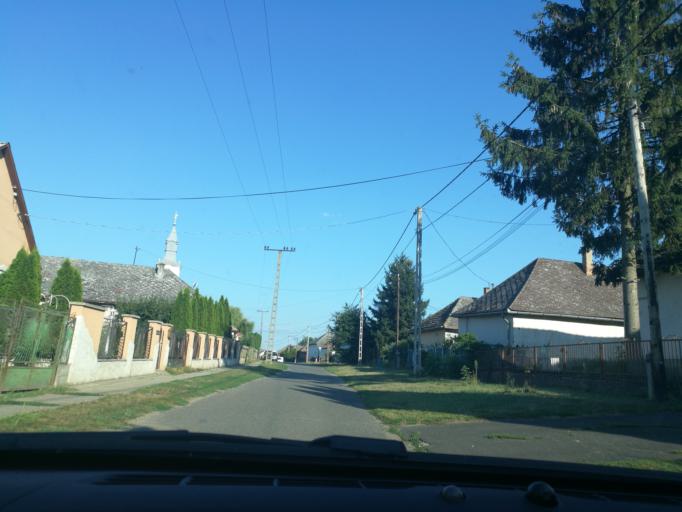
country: HU
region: Szabolcs-Szatmar-Bereg
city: Tiszabercel
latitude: 48.1632
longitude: 21.5946
